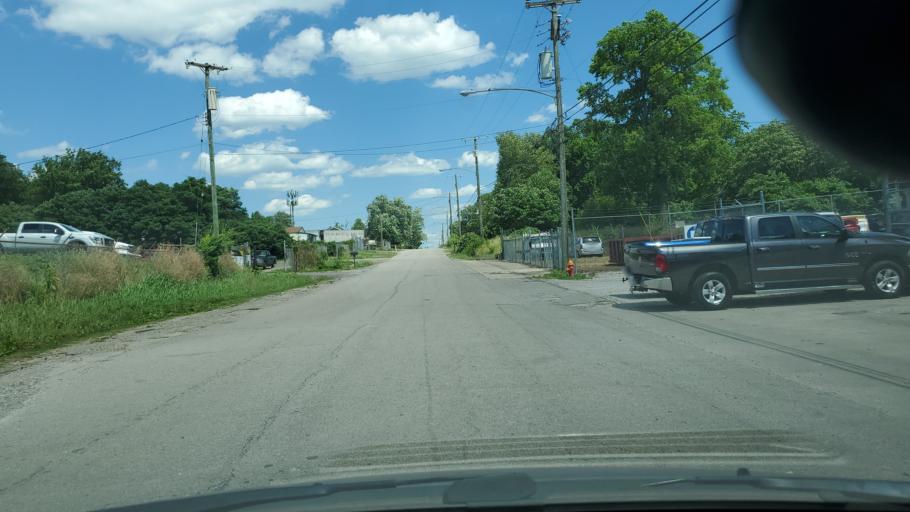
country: US
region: Tennessee
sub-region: Davidson County
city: Nashville
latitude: 36.2018
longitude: -86.7554
